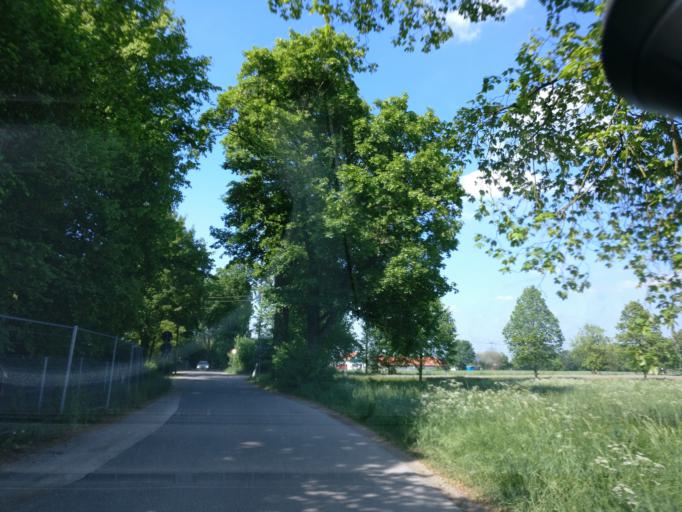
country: DE
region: Bavaria
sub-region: Upper Bavaria
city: Karlsfeld
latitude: 48.1994
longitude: 11.4322
